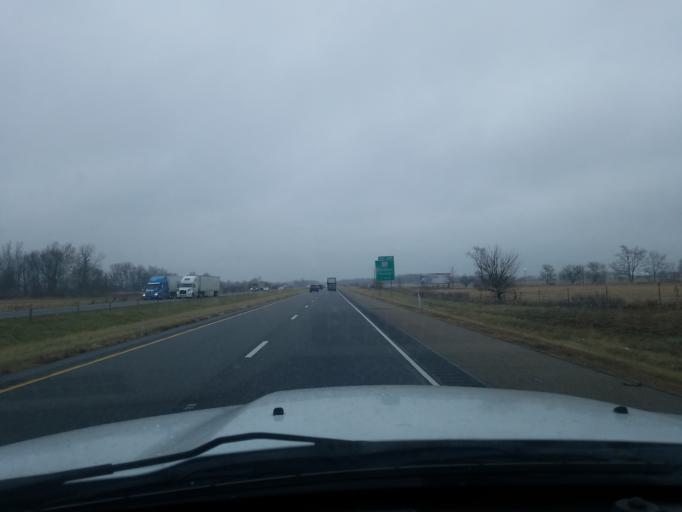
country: US
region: Indiana
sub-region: Delaware County
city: Yorktown
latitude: 40.1984
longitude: -85.5608
